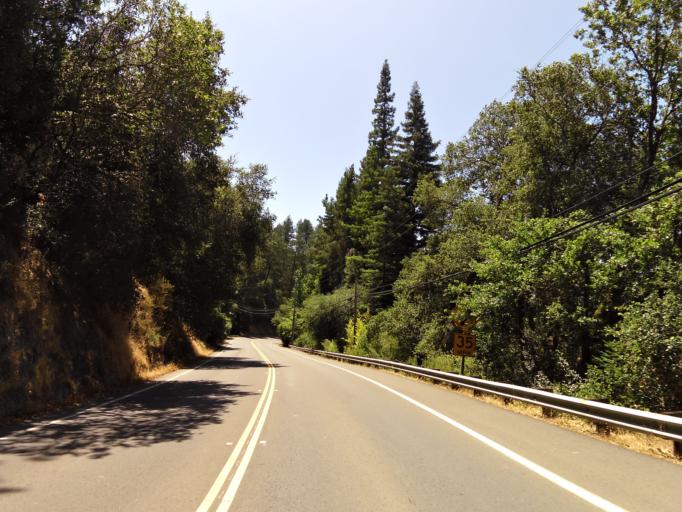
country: US
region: California
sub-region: Napa County
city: Deer Park
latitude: 38.5331
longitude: -122.4907
